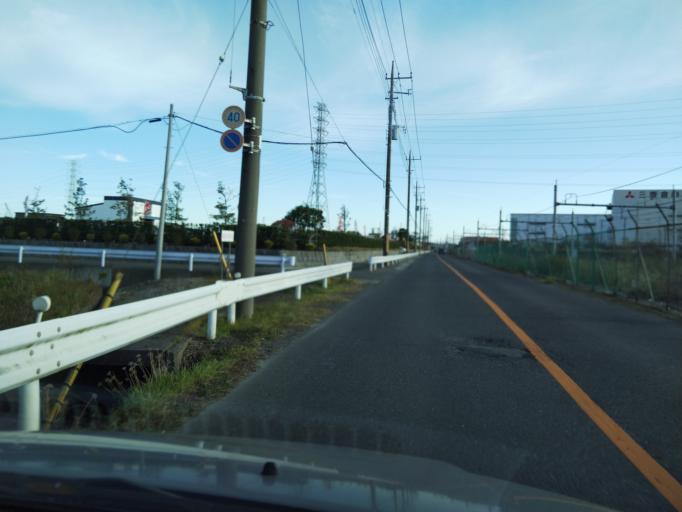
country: JP
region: Saitama
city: Yoshikawa
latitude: 35.8662
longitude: 139.8609
